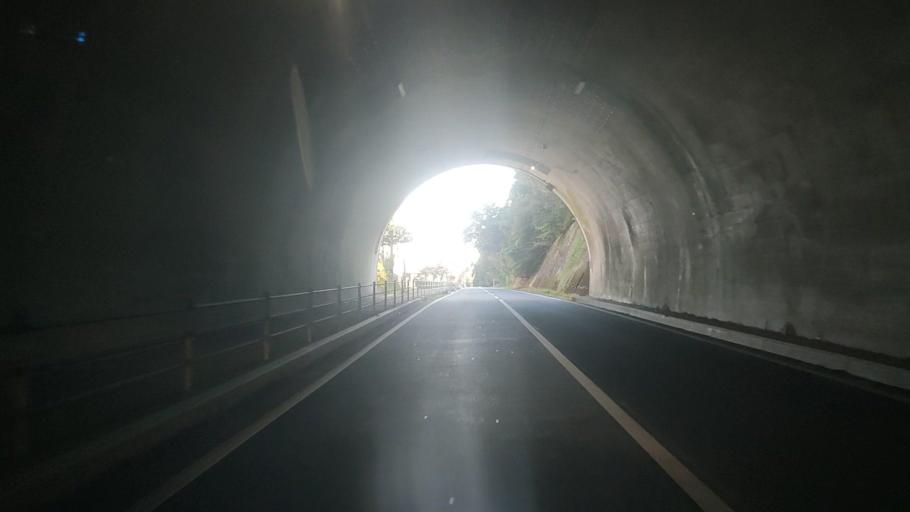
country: JP
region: Oita
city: Saiki
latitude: 32.8005
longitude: 131.9343
